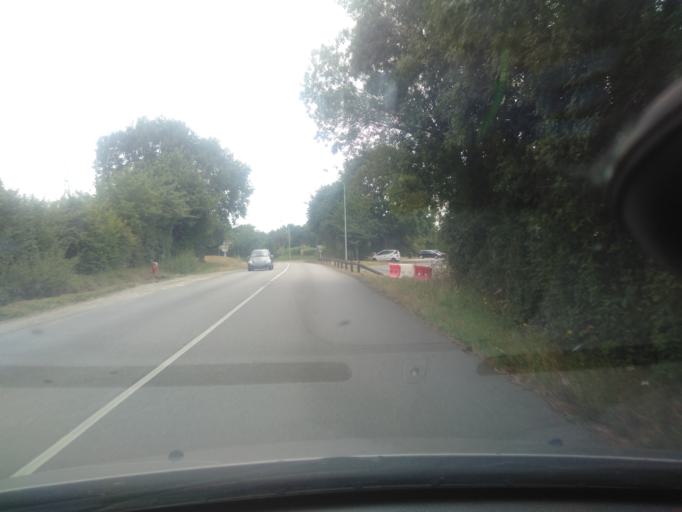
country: FR
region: Pays de la Loire
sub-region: Departement de la Vendee
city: La Roche-sur-Yon
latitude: 46.6919
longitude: -1.4403
